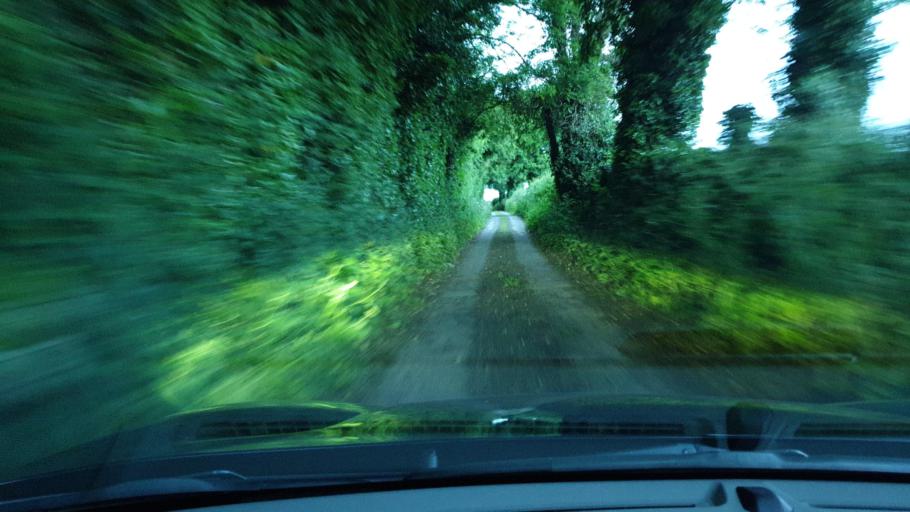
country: IE
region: Leinster
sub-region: An Mhi
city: Duleek
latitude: 53.6002
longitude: -6.3638
